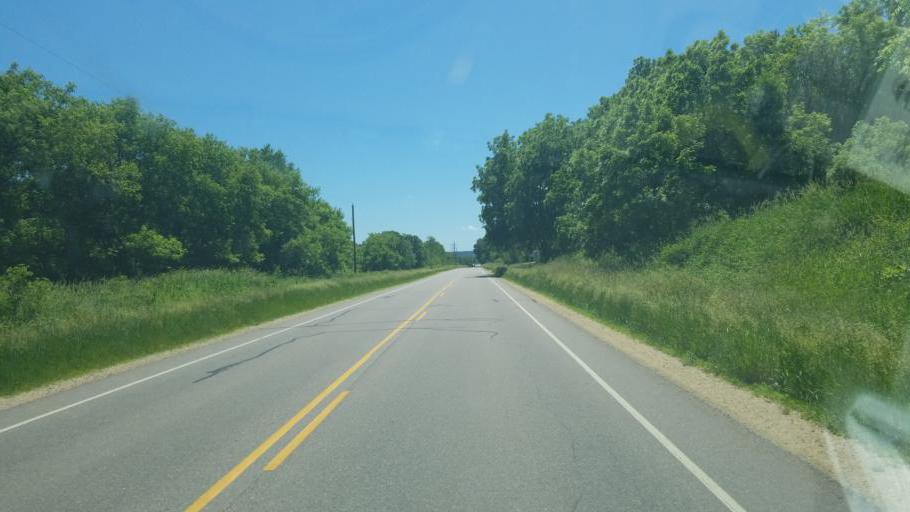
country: US
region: Wisconsin
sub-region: Juneau County
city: Elroy
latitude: 43.7189
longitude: -90.2659
